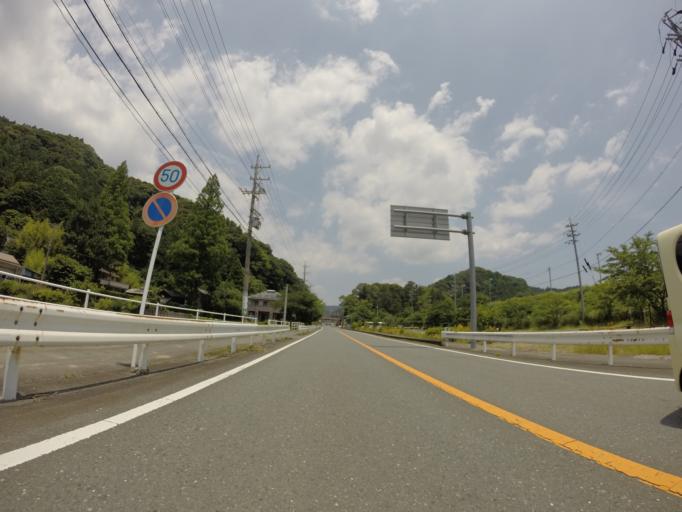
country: JP
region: Shizuoka
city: Kanaya
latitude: 34.7965
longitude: 138.0738
